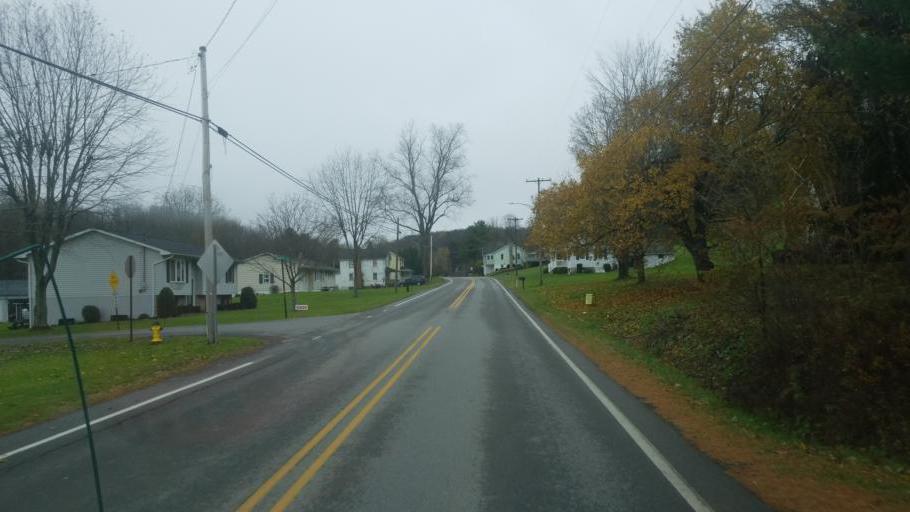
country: US
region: Pennsylvania
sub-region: Elk County
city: Saint Marys
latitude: 41.3601
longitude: -78.6110
